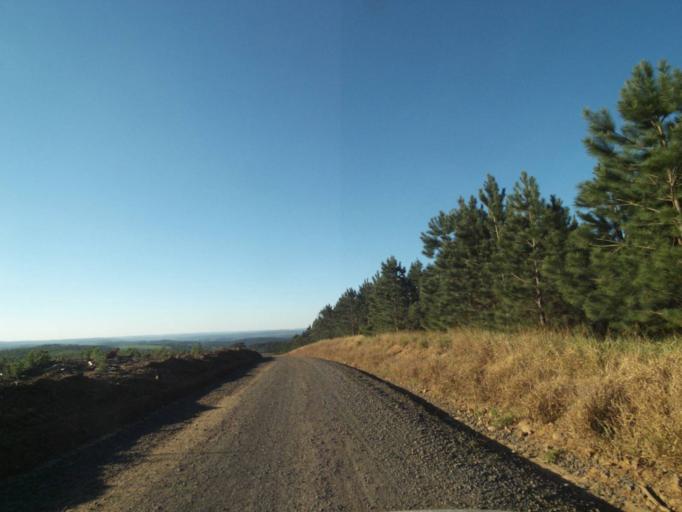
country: BR
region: Parana
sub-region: Telemaco Borba
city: Telemaco Borba
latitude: -24.4532
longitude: -50.6001
